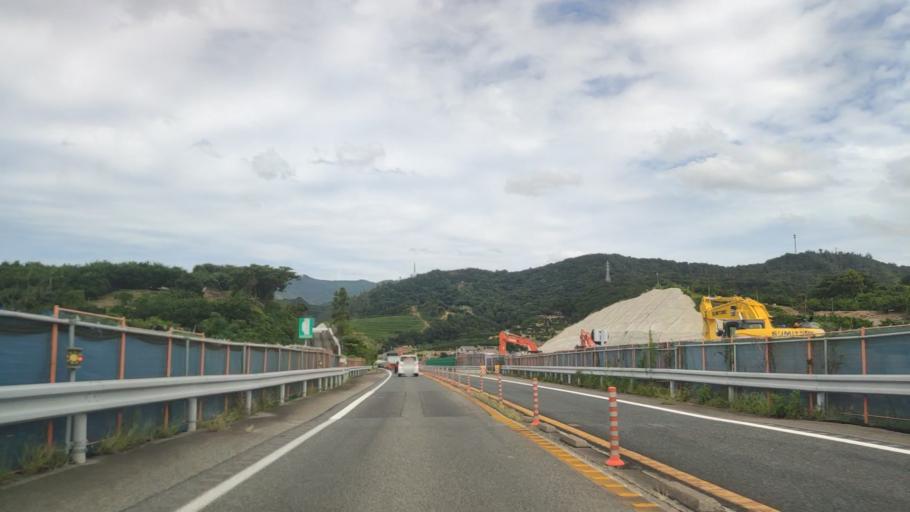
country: JP
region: Wakayama
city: Gobo
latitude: 33.9110
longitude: 135.1944
